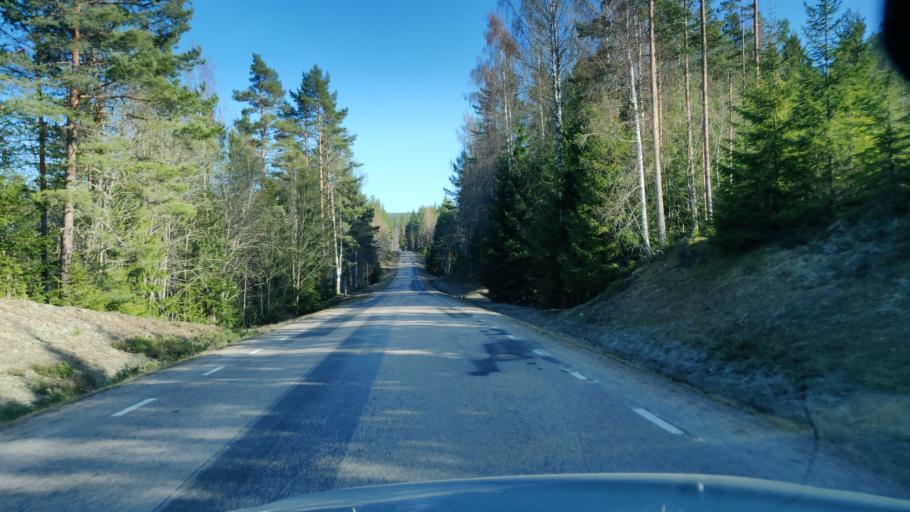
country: SE
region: Vaermland
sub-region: Sunne Kommun
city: Sunne
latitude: 59.9896
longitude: 13.3111
